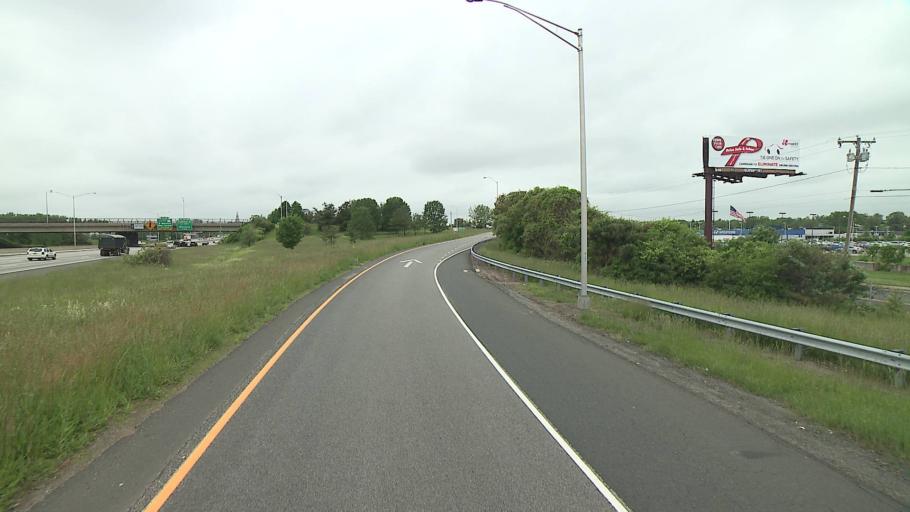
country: US
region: Connecticut
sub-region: Hartford County
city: Hartford
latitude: 41.7891
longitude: -72.6570
